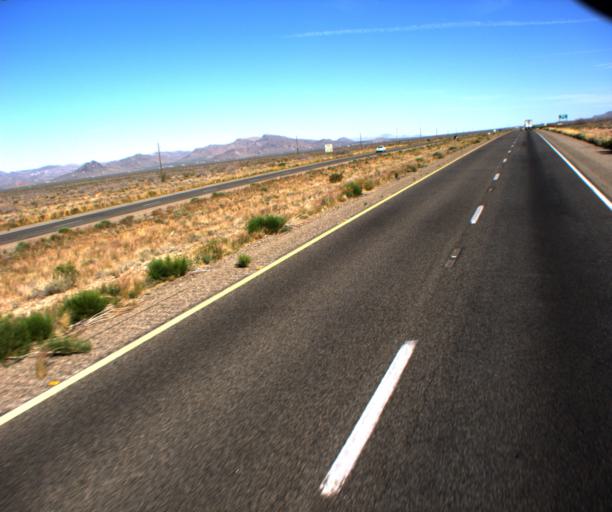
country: US
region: Arizona
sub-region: Mohave County
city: Golden Valley
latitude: 35.2873
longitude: -114.1797
